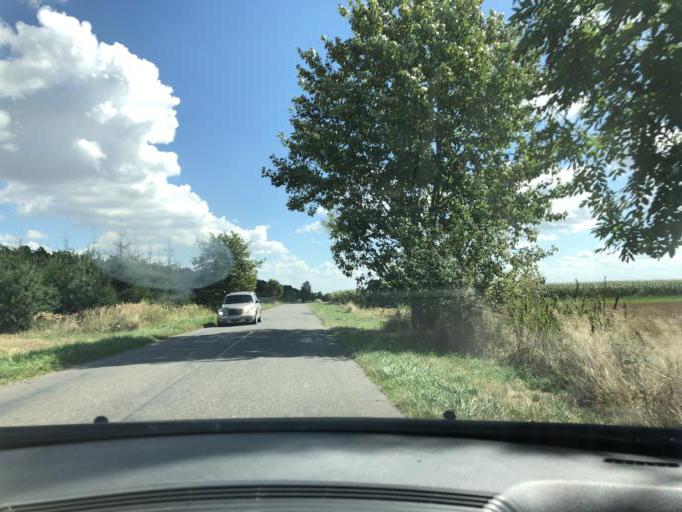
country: PL
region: Lodz Voivodeship
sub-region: Powiat wieruszowski
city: Czastary
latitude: 51.2601
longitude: 18.3438
